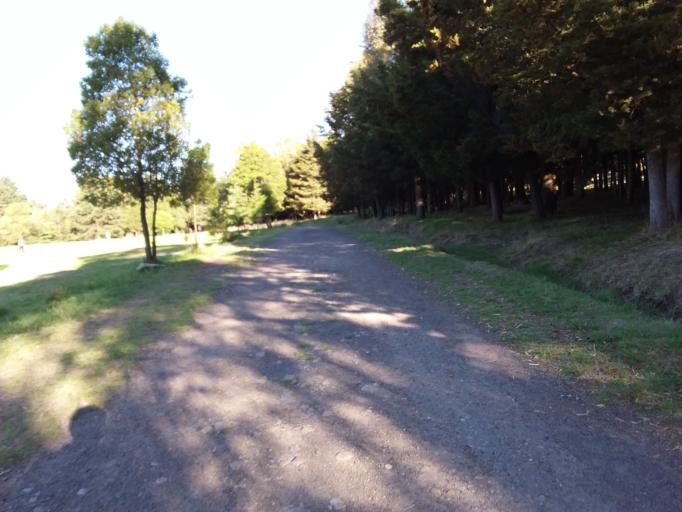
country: MX
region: Mexico
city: San Marcos Yachihuacaltepec
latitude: 19.3115
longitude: -99.6885
